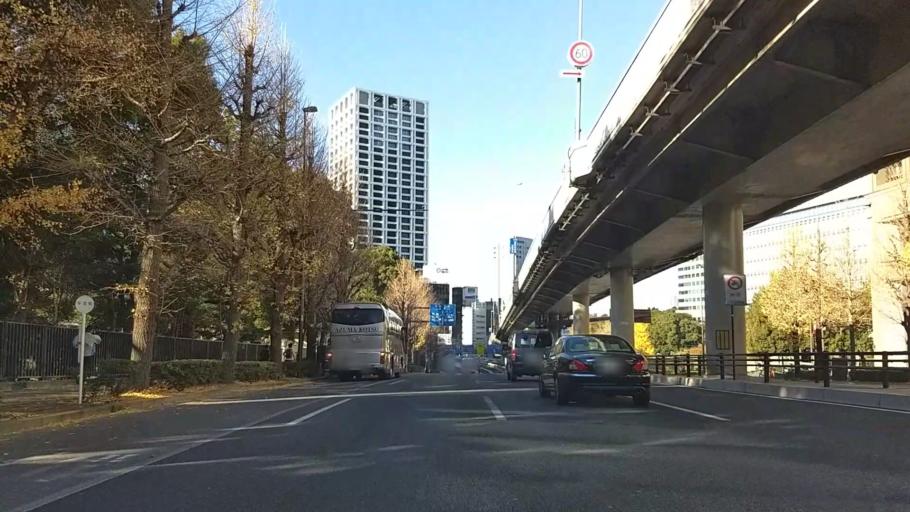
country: JP
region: Tokyo
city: Tokyo
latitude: 35.6787
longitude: 139.7398
